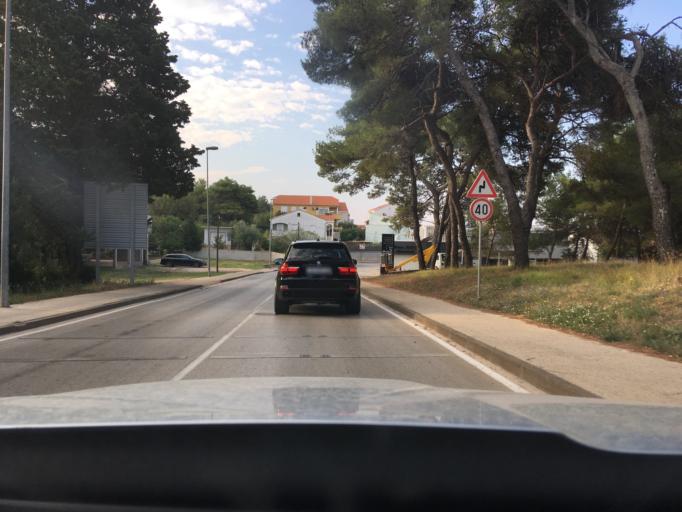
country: HR
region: Zadarska
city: Zadar
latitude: 44.1375
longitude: 15.2291
